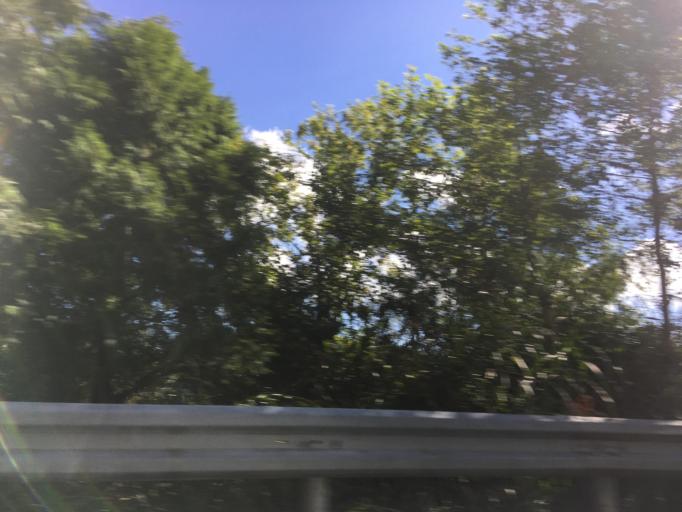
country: TW
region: Taiwan
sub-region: Yilan
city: Yilan
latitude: 24.5102
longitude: 121.5694
